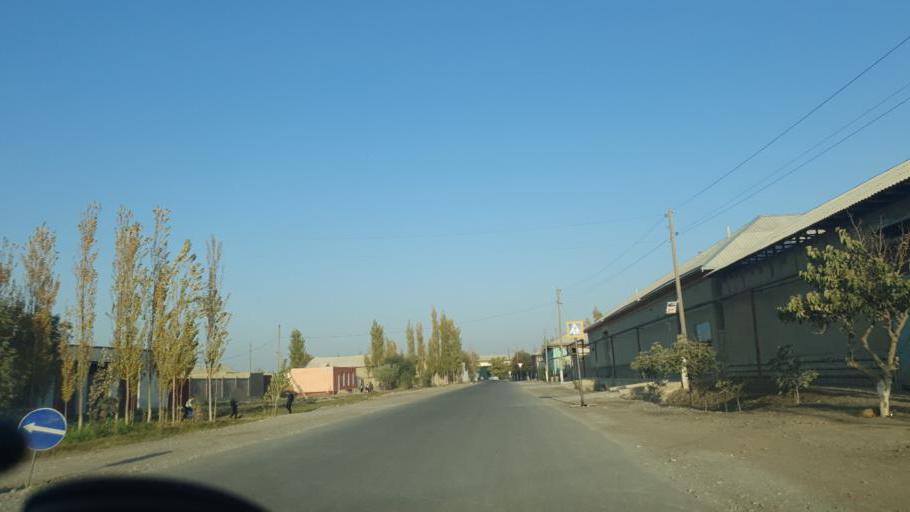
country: UZ
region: Fergana
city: Beshariq
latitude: 40.4675
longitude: 70.5607
